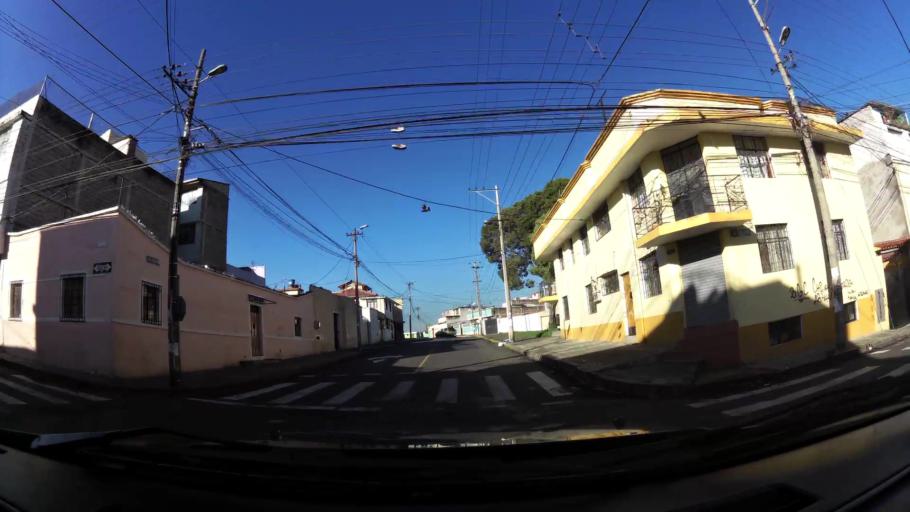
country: EC
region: Pichincha
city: Quito
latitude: -0.2427
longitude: -78.5151
